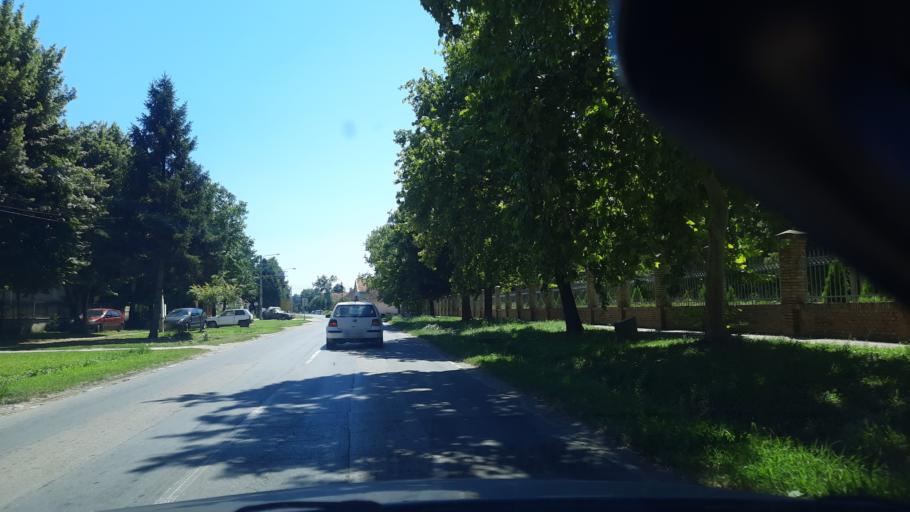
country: RS
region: Autonomna Pokrajina Vojvodina
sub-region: Juznobanatski Okrug
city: Kovin
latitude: 44.7571
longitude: 20.9837
